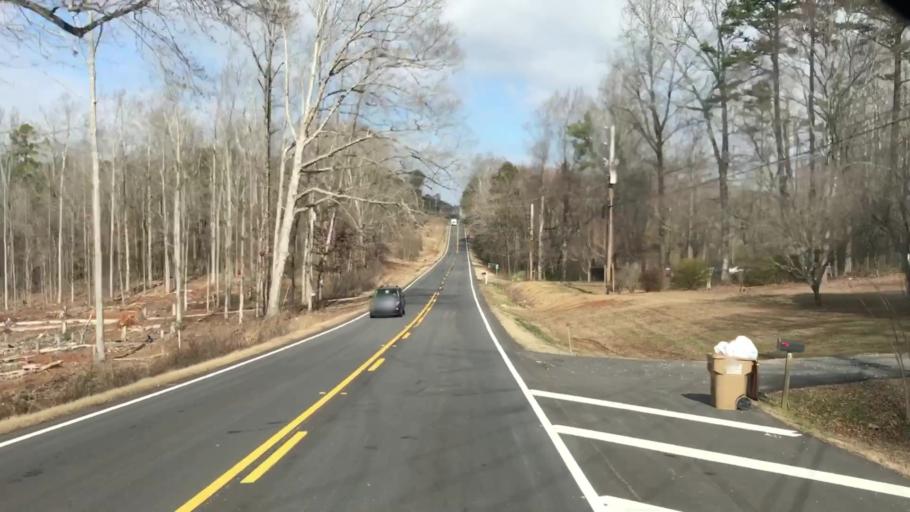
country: US
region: Georgia
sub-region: Jackson County
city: Braselton
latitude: 34.1480
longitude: -83.8375
